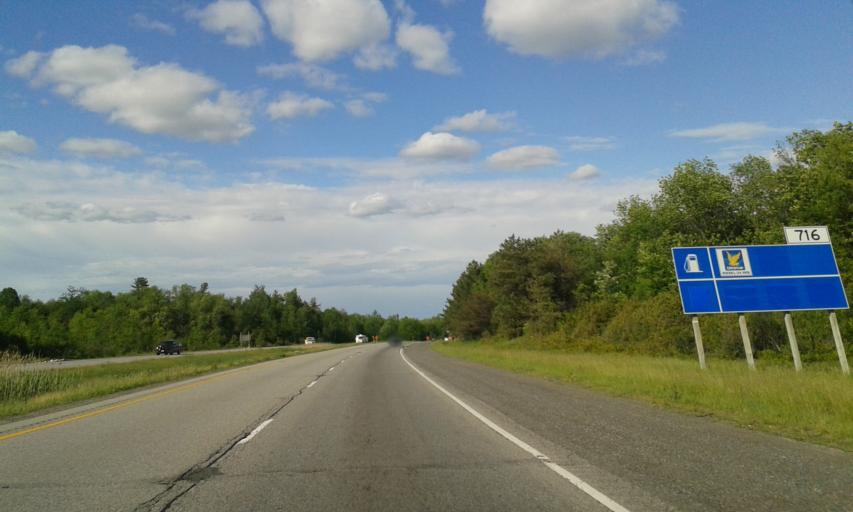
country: CA
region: Ontario
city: Prescott
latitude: 44.7115
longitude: -75.5558
